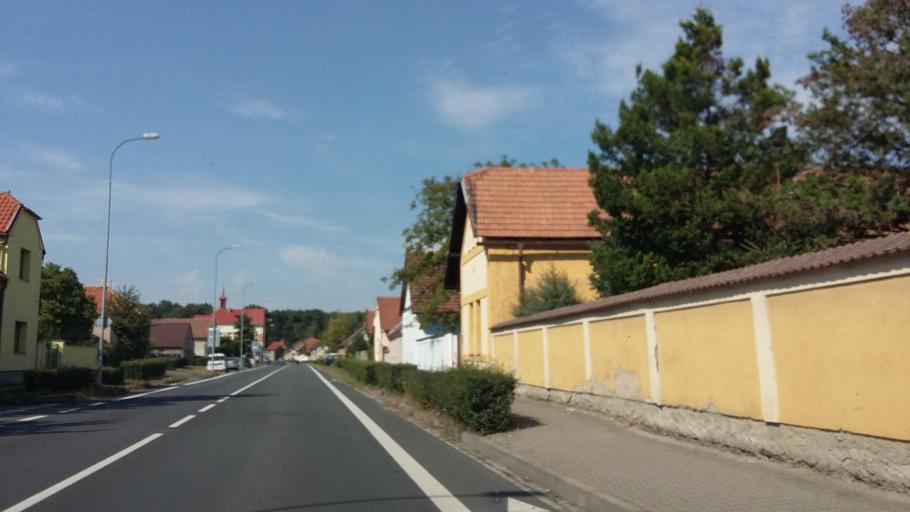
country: CZ
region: Central Bohemia
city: Velky Osek
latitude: 50.0973
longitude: 15.1863
